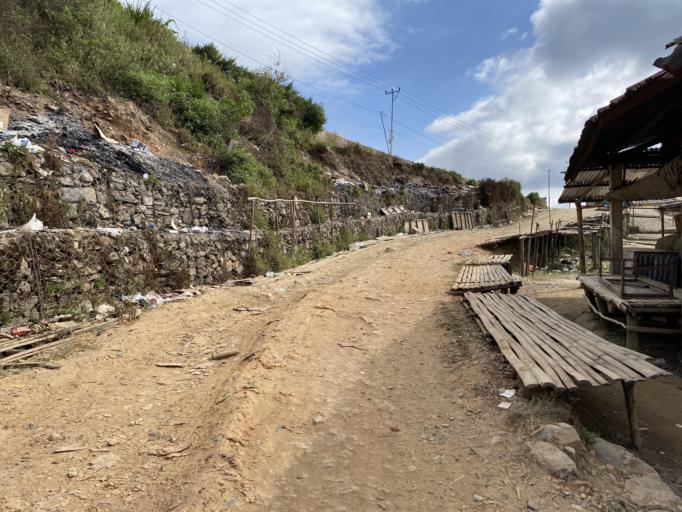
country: TL
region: Ermera
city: Gleno
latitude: -8.8370
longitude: 125.4312
